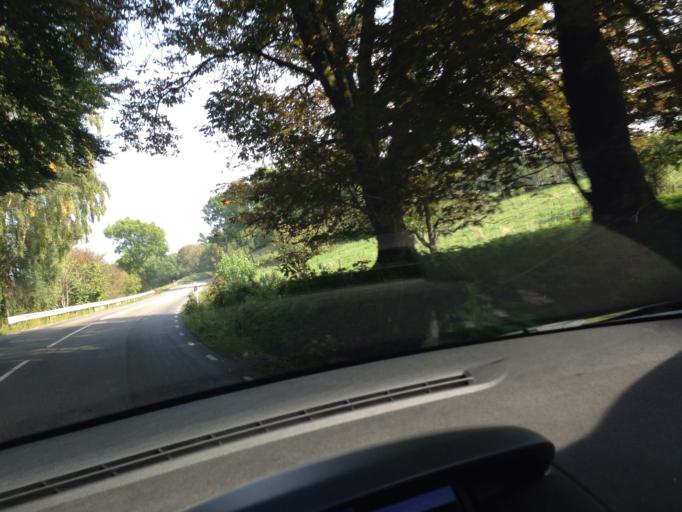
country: SE
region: Skane
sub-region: Bastads Kommun
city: Bastad
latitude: 56.4377
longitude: 12.7997
